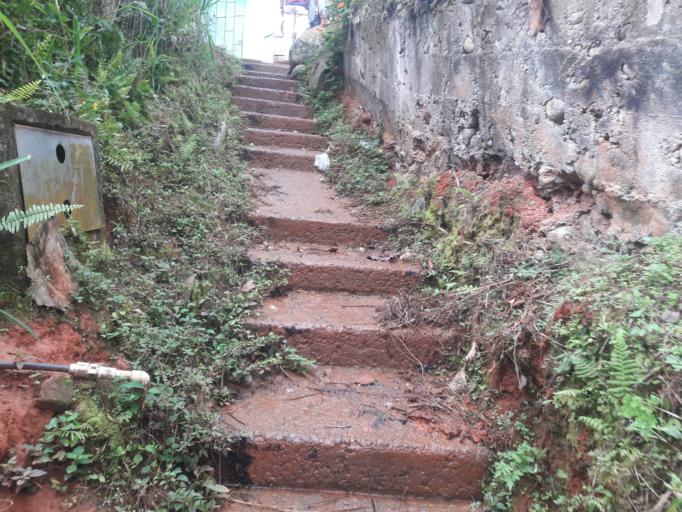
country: CO
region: Valle del Cauca
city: Cali
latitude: 3.4692
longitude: -76.6311
